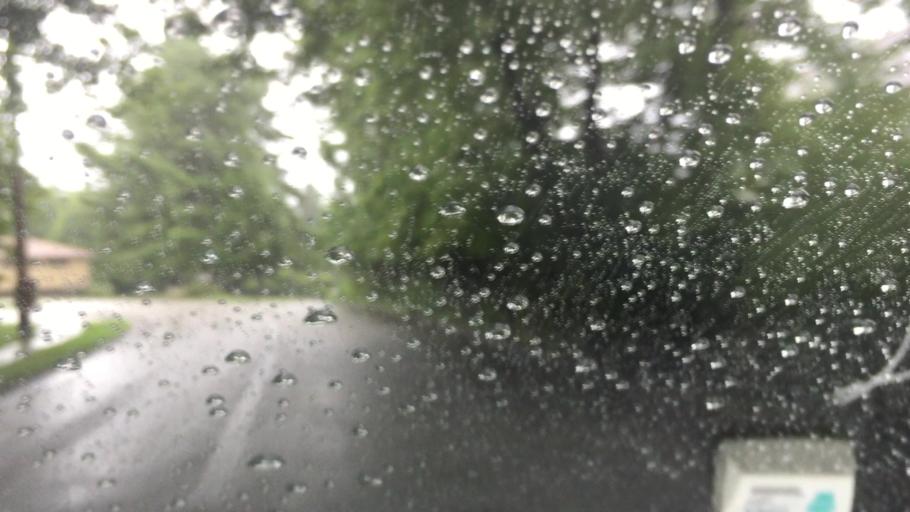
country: US
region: Pennsylvania
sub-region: Allegheny County
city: Franklin Park
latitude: 40.5931
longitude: -80.0342
